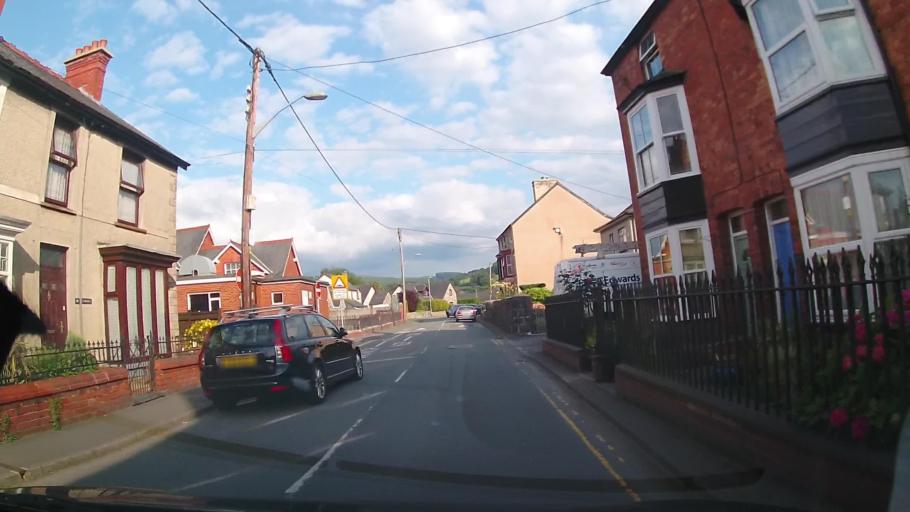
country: GB
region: Wales
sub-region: Gwynedd
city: Bala
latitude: 52.9086
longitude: -3.5961
